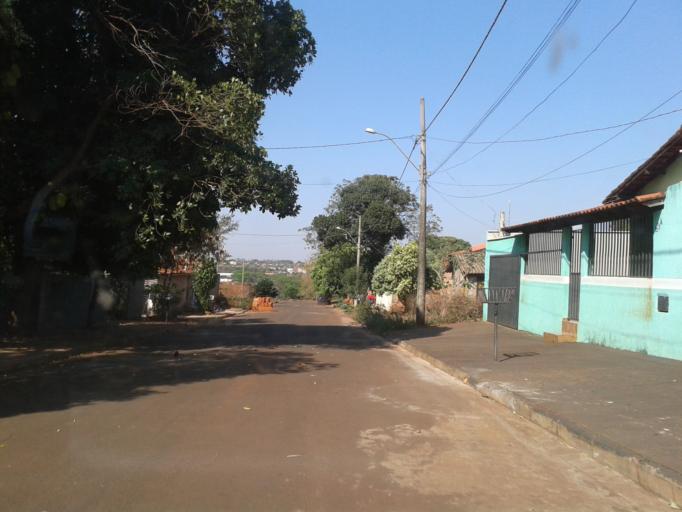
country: BR
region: Minas Gerais
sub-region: Ituiutaba
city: Ituiutaba
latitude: -18.9625
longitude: -49.4827
